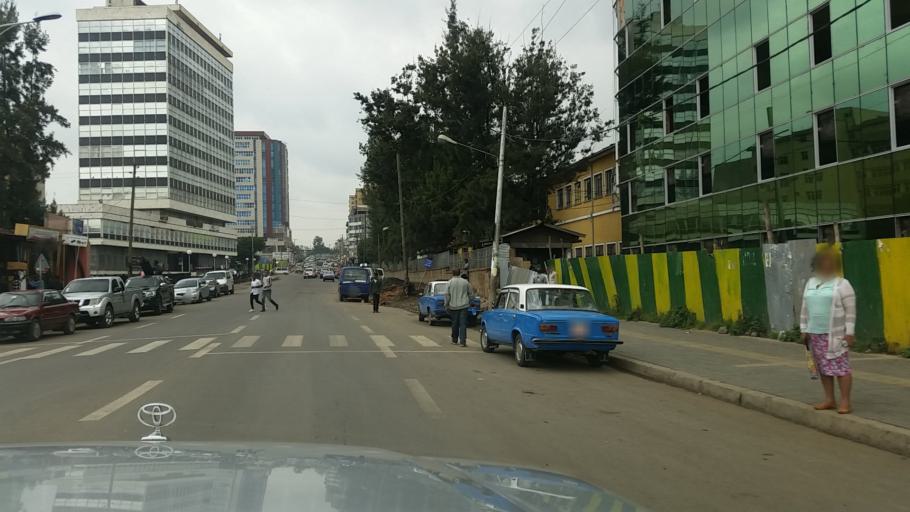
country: ET
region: Adis Abeba
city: Addis Ababa
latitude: 9.0120
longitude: 38.7499
